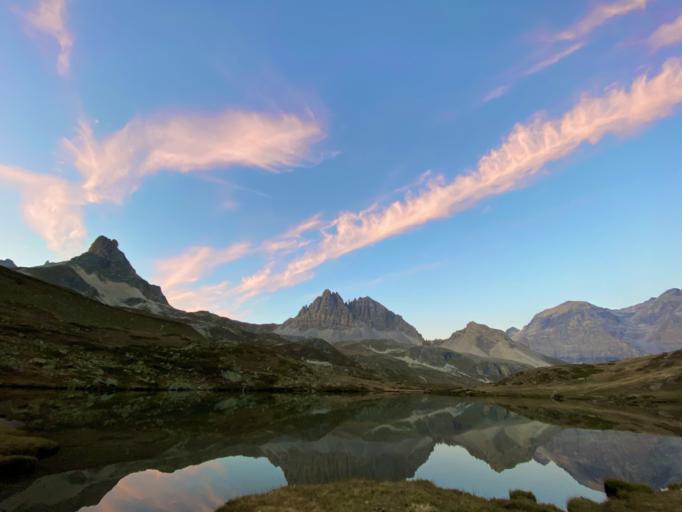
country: IT
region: Piedmont
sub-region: Provincia di Torino
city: Bardonecchia
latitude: 45.0862
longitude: 6.5804
